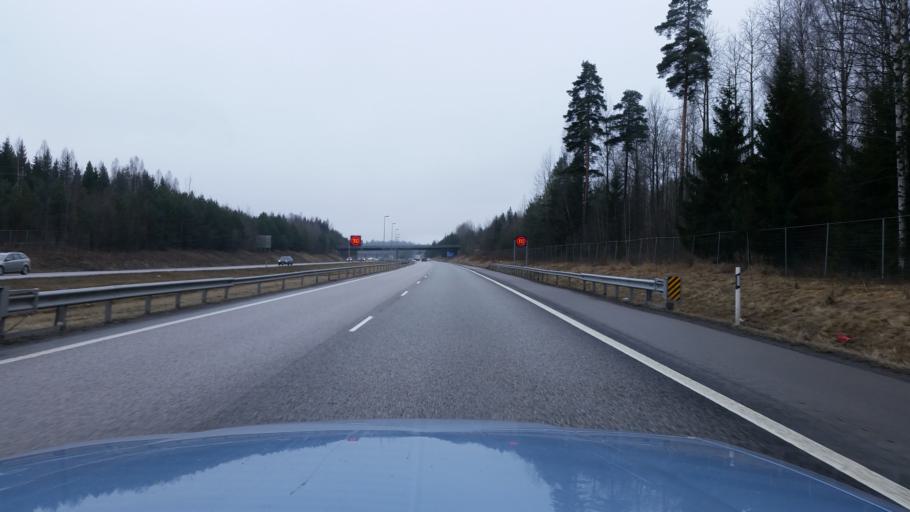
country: FI
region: Uusimaa
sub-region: Helsinki
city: Nurmijaervi
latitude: 60.3641
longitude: 24.8087
